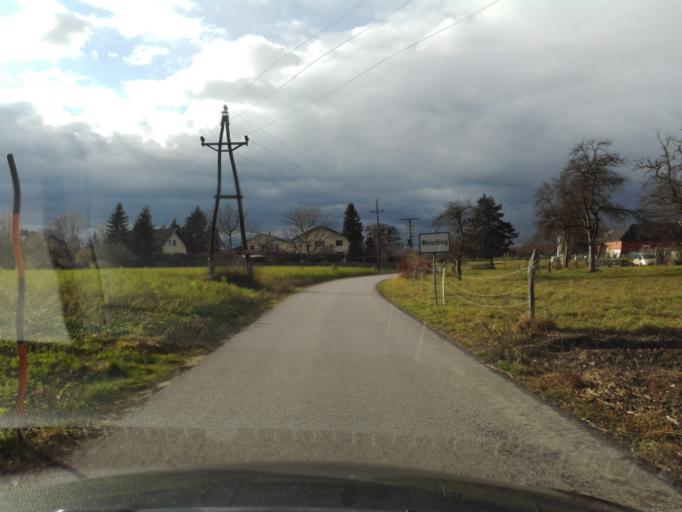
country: AT
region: Lower Austria
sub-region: Politischer Bezirk Amstetten
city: Strengberg
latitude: 48.1802
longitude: 14.6829
